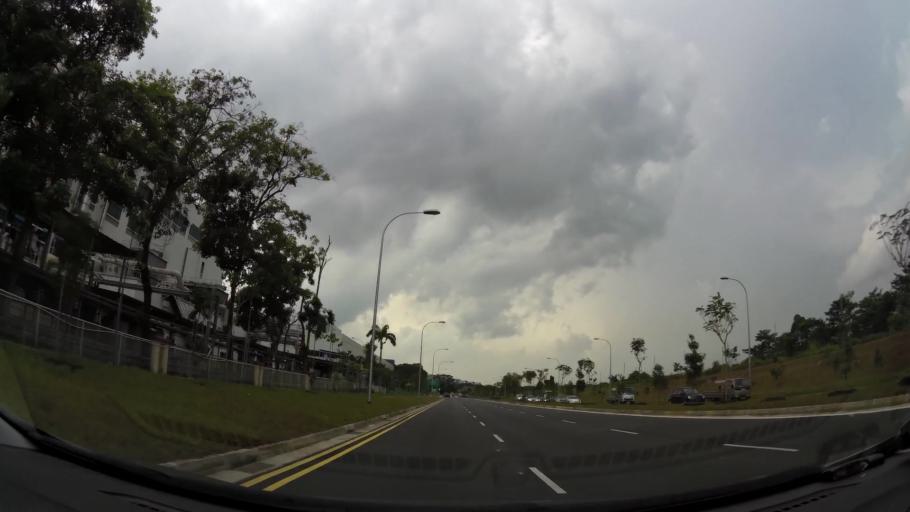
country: MY
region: Johor
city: Kampung Pasir Gudang Baru
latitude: 1.4405
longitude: 103.8431
